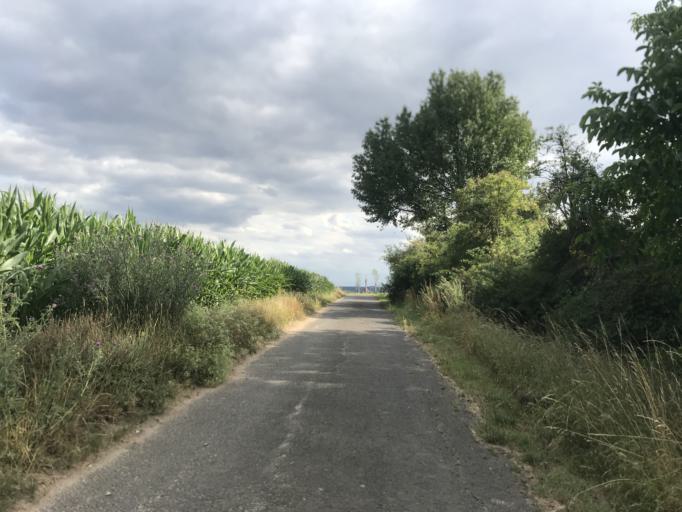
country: DE
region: Hesse
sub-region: Regierungsbezirk Darmstadt
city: Hochheim am Main
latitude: 50.0206
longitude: 8.3121
